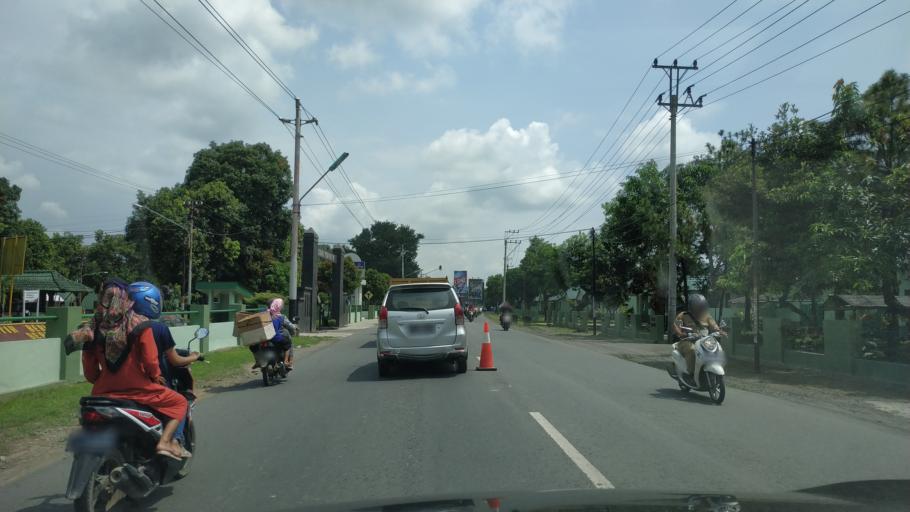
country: ID
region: Central Java
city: Adiwerna
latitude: -6.9433
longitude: 109.1264
